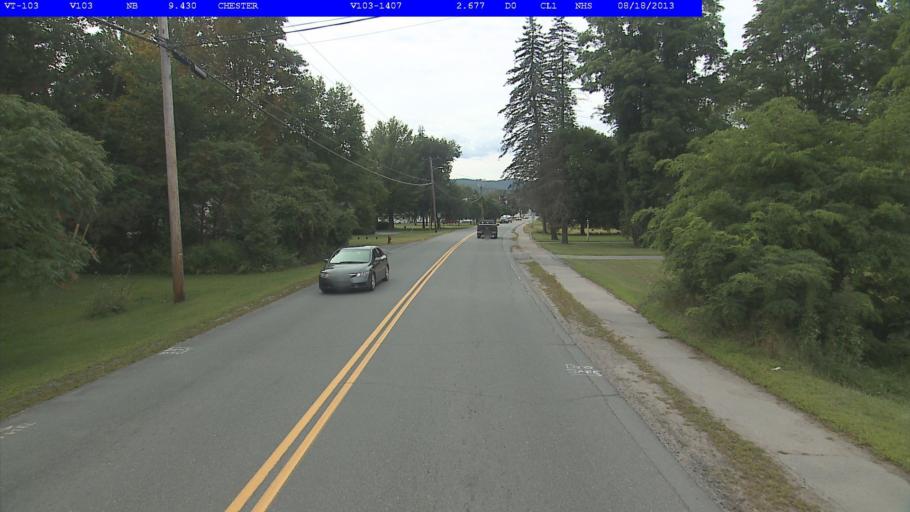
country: US
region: Vermont
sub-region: Windsor County
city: Chester
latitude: 43.2599
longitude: -72.5908
